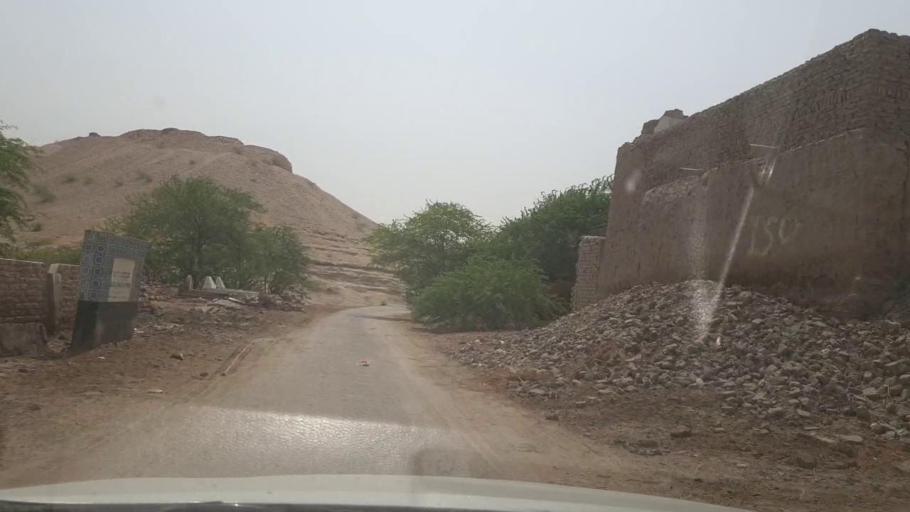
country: PK
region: Sindh
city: Kot Diji
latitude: 27.3455
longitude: 68.7121
